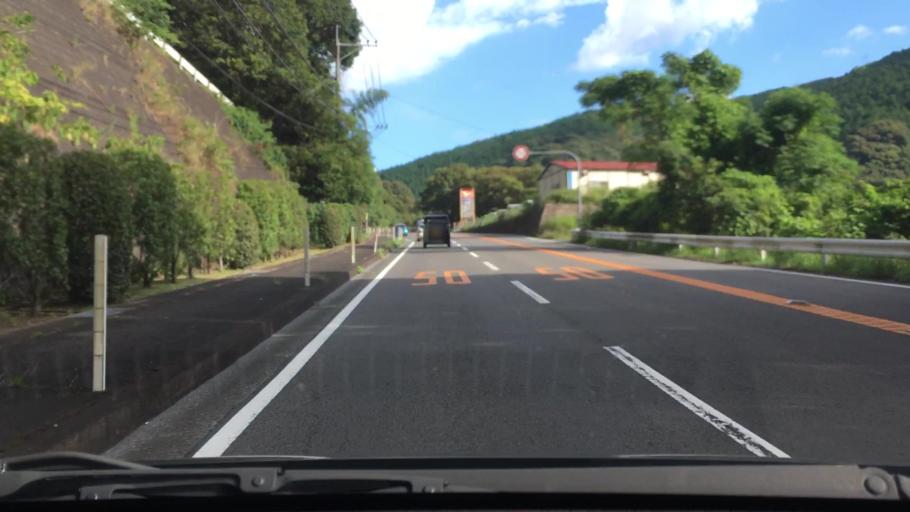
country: JP
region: Nagasaki
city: Togitsu
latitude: 32.8209
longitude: 129.8002
